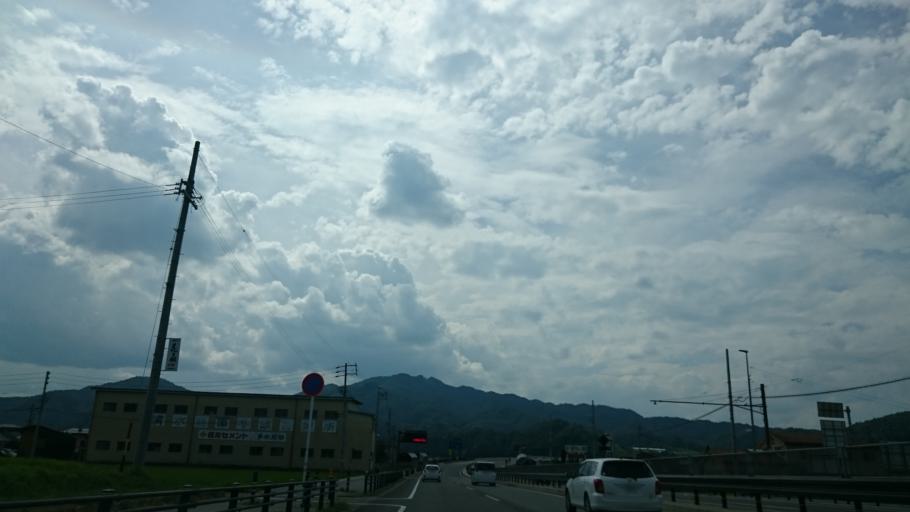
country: JP
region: Gifu
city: Takayama
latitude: 36.1621
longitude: 137.2414
